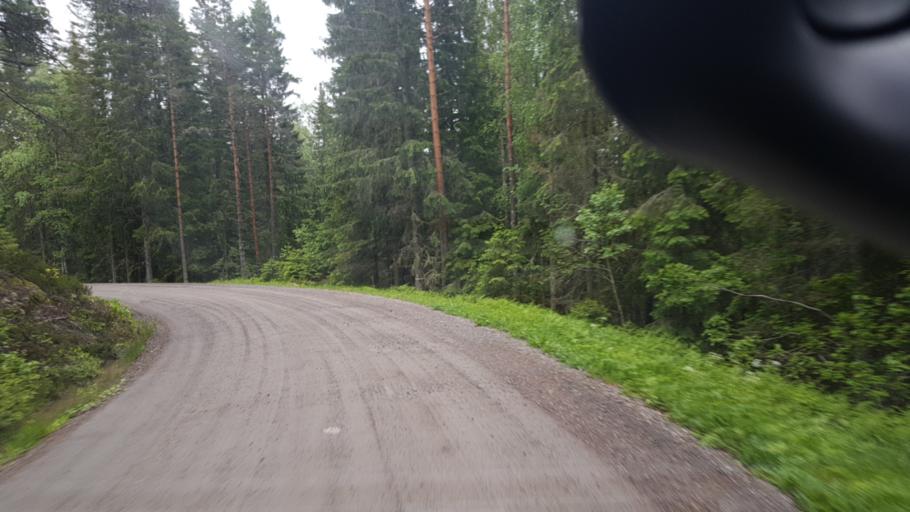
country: NO
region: Ostfold
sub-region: Romskog
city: Romskog
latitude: 59.7120
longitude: 12.0242
